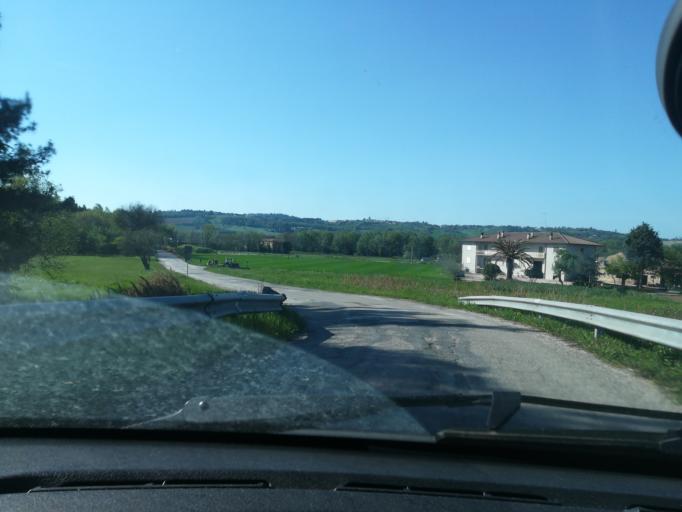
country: IT
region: The Marches
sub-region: Provincia di Macerata
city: Zona Industriale
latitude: 43.2674
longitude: 13.4931
